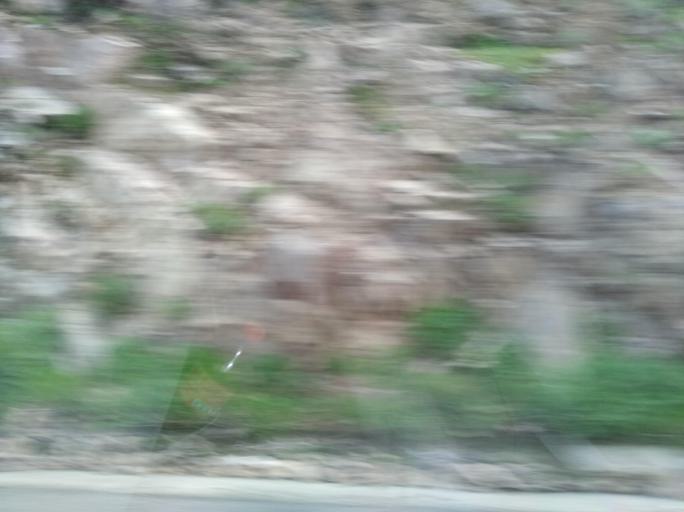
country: CL
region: Valparaiso
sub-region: Provincia de San Felipe
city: Llaillay
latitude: -33.0721
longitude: -70.9703
